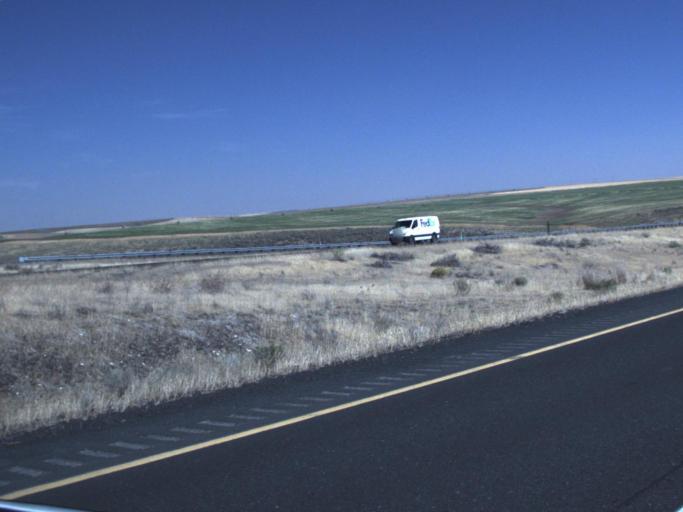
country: US
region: Washington
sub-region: Grant County
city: Warden
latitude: 47.0858
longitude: -118.8395
